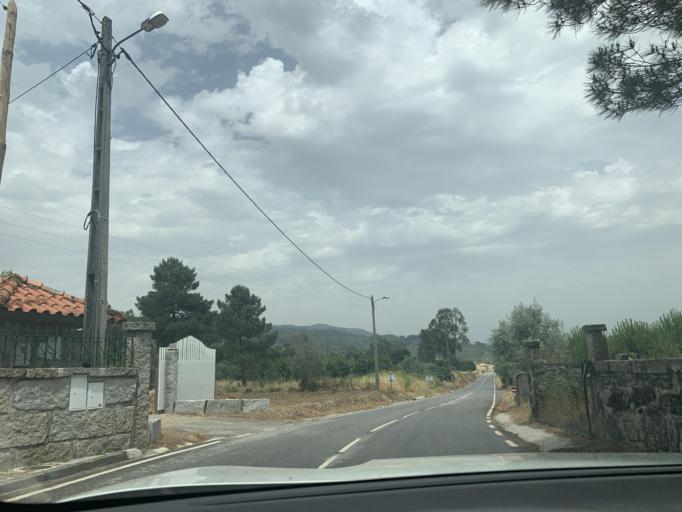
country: PT
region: Viseu
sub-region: Mangualde
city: Mangualde
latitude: 40.5634
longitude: -7.6844
